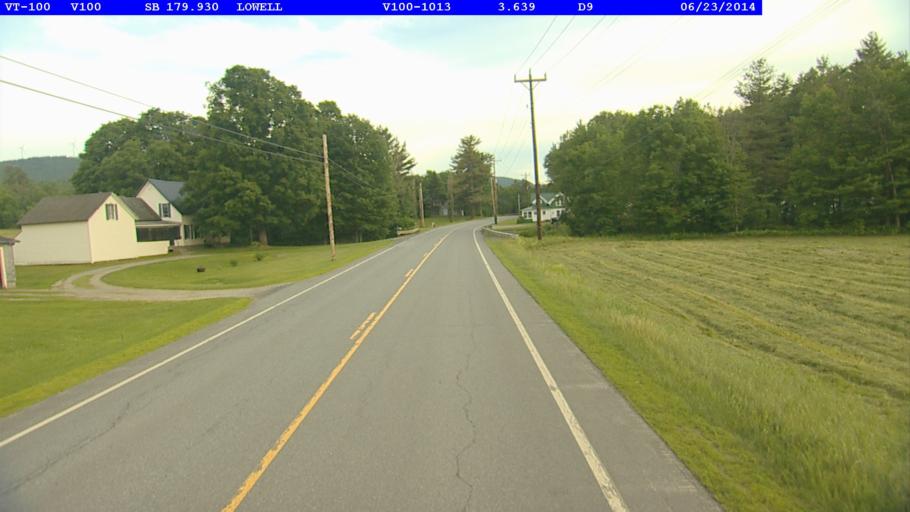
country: US
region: Vermont
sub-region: Lamoille County
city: Hyde Park
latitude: 44.7885
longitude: -72.4487
